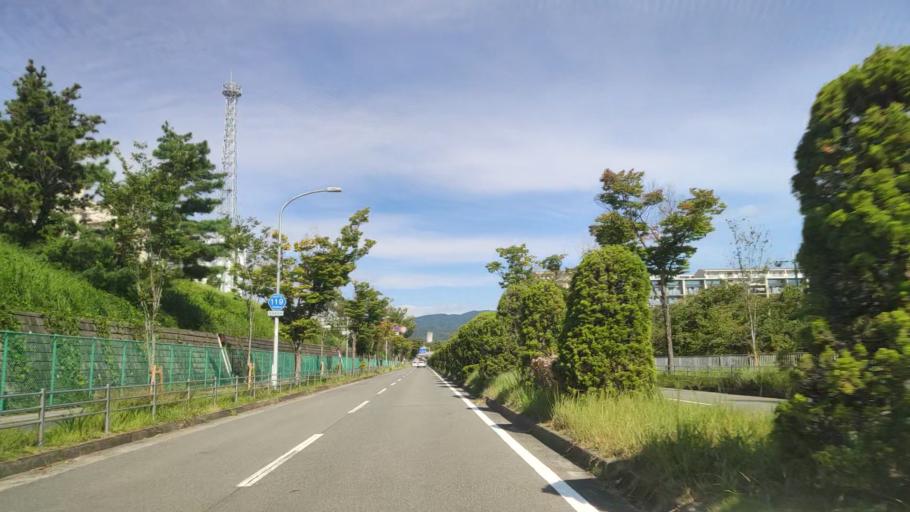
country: JP
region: Osaka
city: Mino
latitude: 34.8172
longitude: 135.5128
